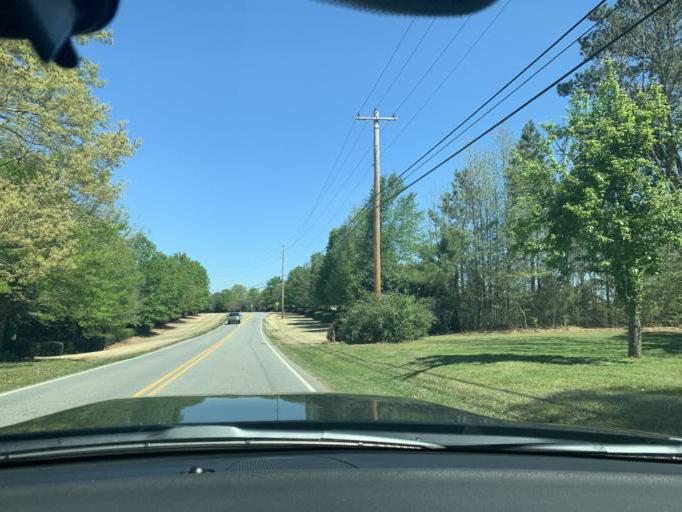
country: US
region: Georgia
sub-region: Forsyth County
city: Cumming
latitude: 34.1750
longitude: -84.1682
